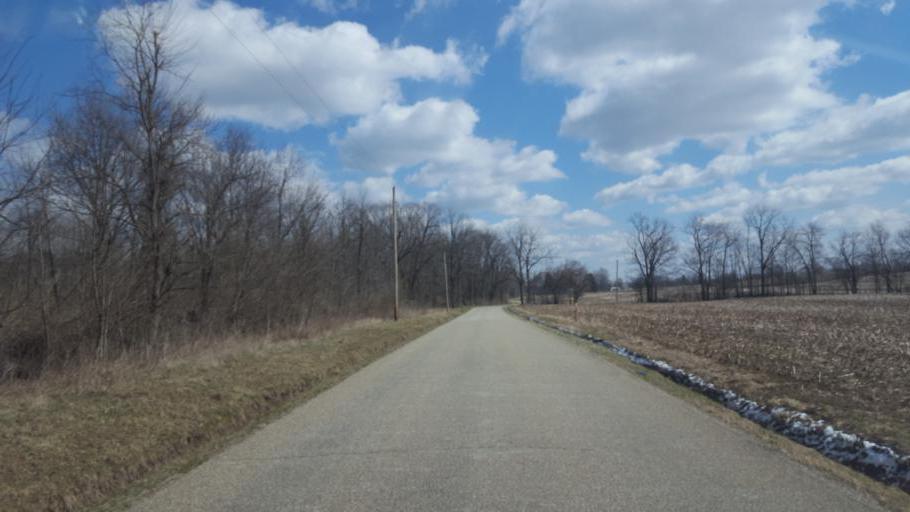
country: US
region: Ohio
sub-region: Knox County
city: Mount Vernon
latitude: 40.3533
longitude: -82.5290
